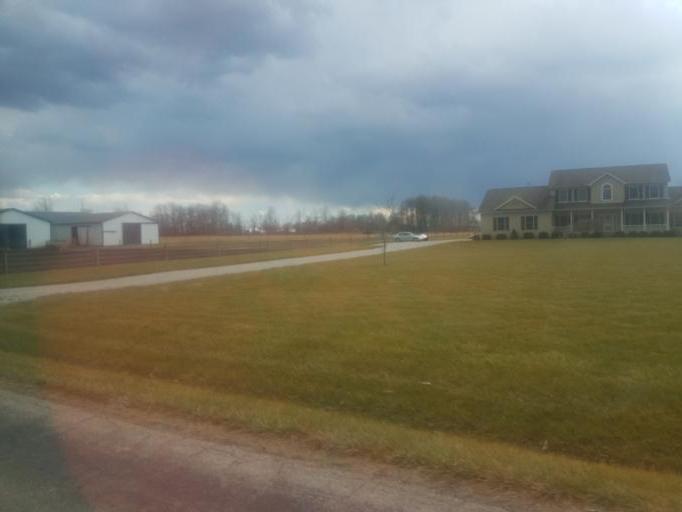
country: US
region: Ohio
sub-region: Marion County
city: Prospect
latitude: 40.4706
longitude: -83.1163
